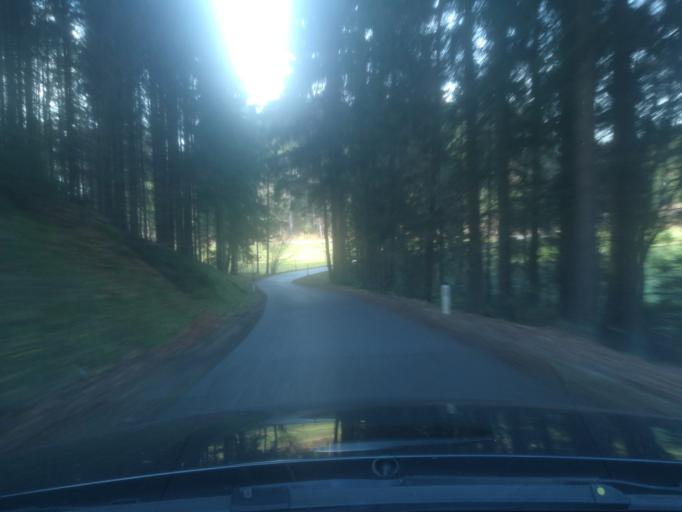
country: AT
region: Upper Austria
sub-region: Politischer Bezirk Perg
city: Perg
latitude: 48.3218
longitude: 14.6605
